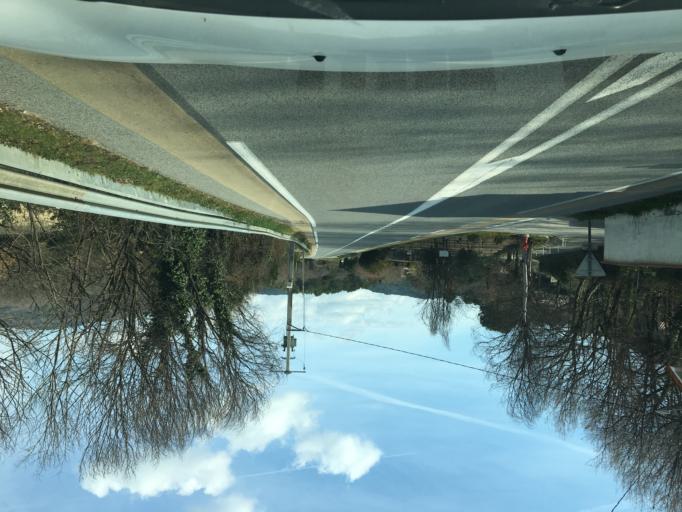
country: FR
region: Provence-Alpes-Cote d'Azur
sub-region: Departement du Var
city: Figanieres
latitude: 43.5616
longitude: 6.5122
